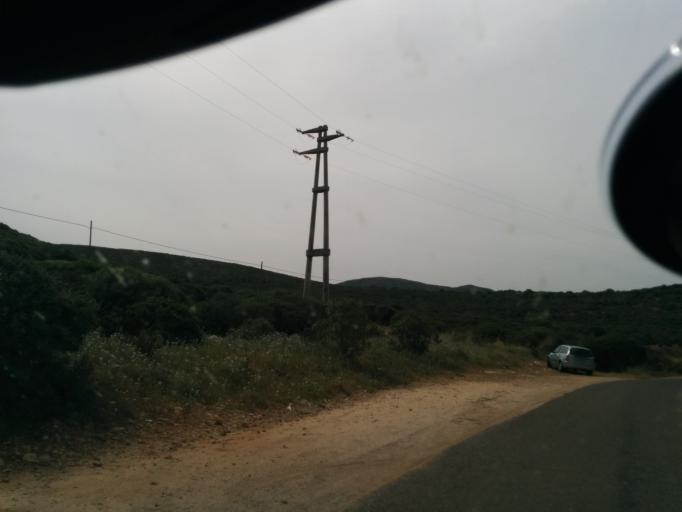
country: IT
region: Sardinia
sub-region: Provincia di Carbonia-Iglesias
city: Sant'Antioco
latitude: 39.0090
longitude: 8.4488
